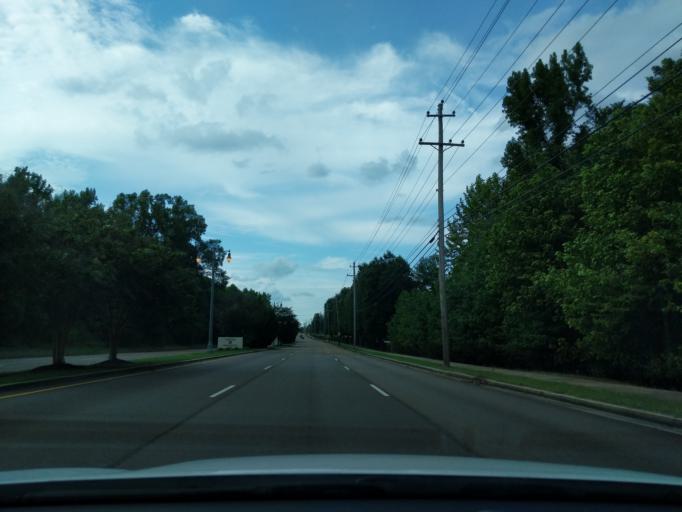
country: US
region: Tennessee
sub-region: Shelby County
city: Germantown
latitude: 35.0351
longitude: -89.7597
